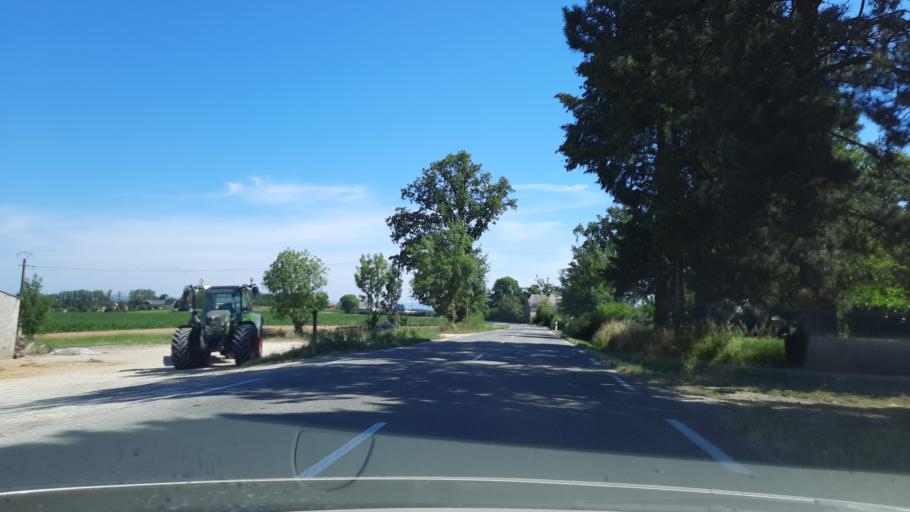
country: FR
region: Midi-Pyrenees
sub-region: Departement de l'Aveyron
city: Montbazens
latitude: 44.4352
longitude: 2.1949
